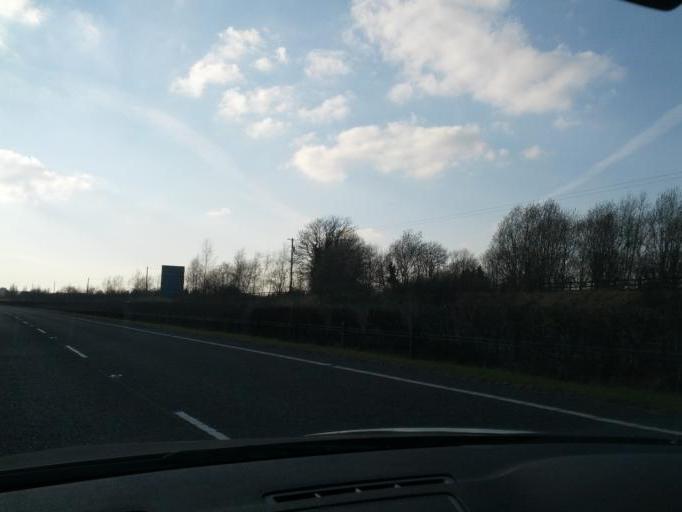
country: IE
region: Leinster
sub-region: Kildare
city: Cherryville
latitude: 53.1547
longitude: -6.9434
